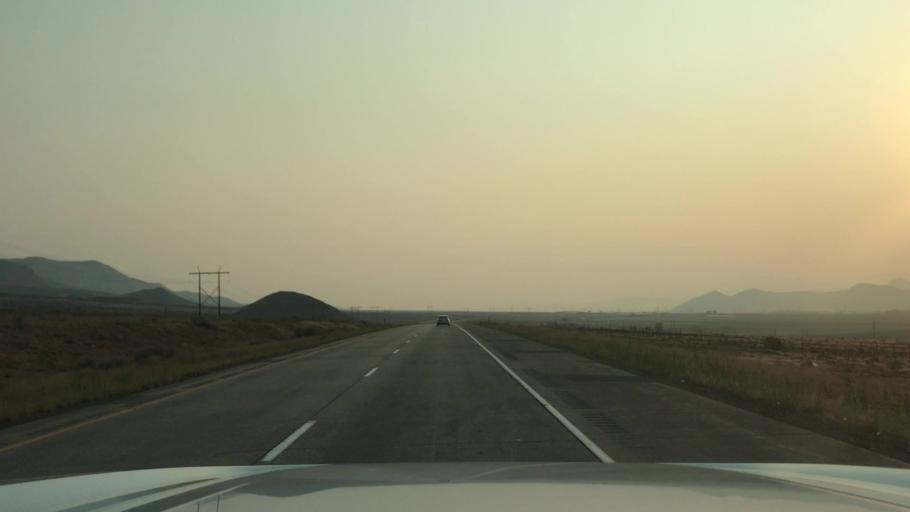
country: US
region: Utah
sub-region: Sevier County
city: Richfield
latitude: 38.8242
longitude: -112.0419
